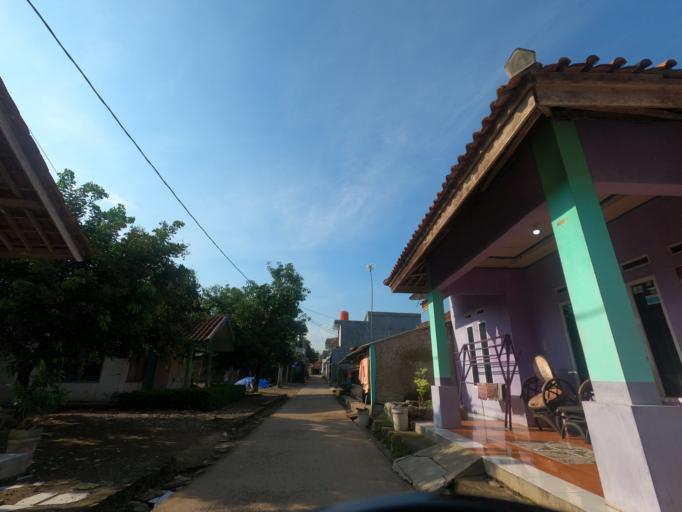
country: ID
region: West Java
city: Pamanukan
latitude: -6.5560
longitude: 107.8259
